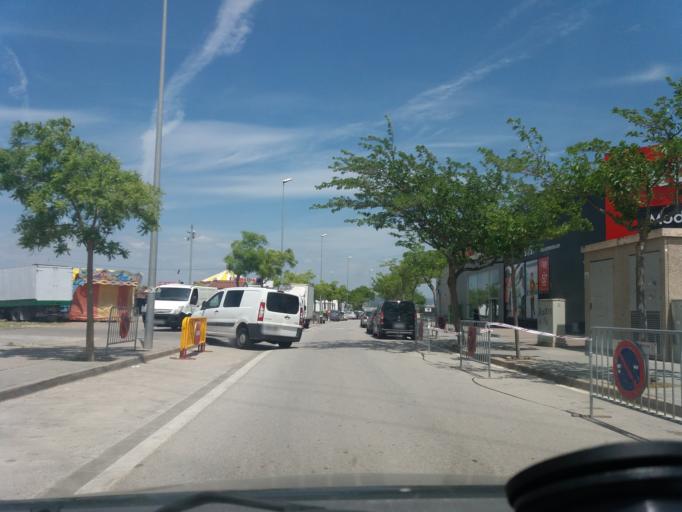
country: ES
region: Catalonia
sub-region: Provincia de Barcelona
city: Manresa
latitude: 41.7249
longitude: 1.8490
